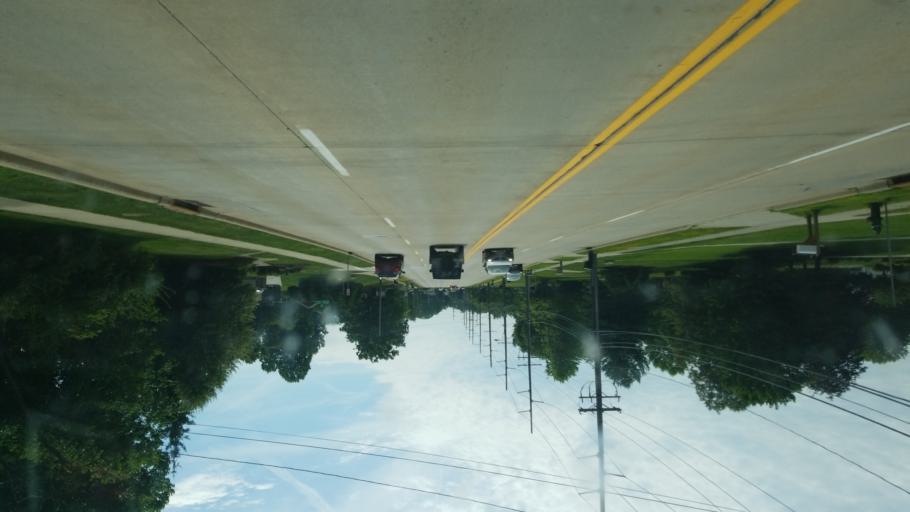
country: US
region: Ohio
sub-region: Cuyahoga County
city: Strongsville
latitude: 41.3126
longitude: -81.8455
